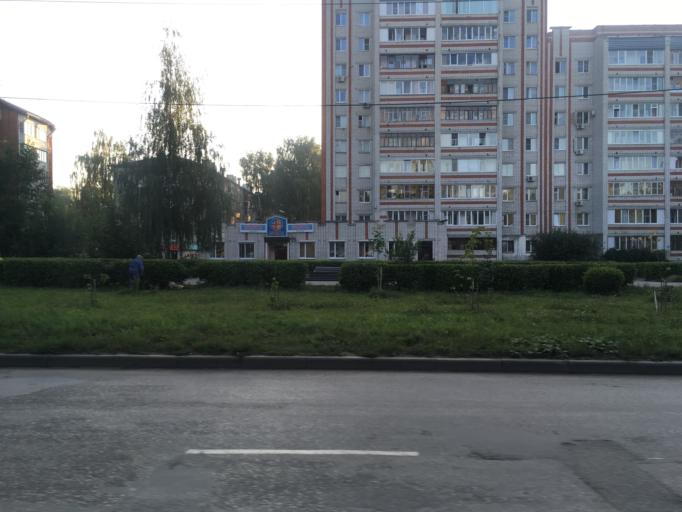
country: RU
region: Mariy-El
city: Yoshkar-Ola
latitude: 56.6501
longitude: 47.8748
